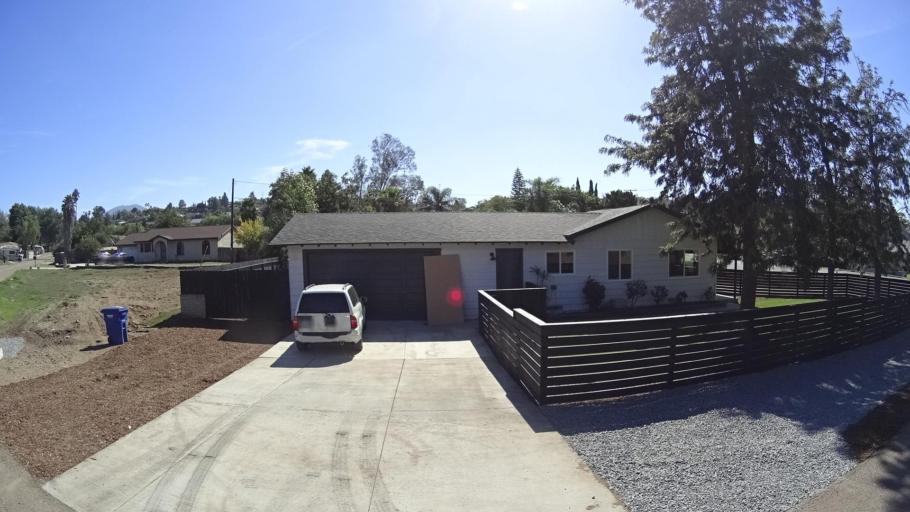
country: US
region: California
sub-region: San Diego County
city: Casa de Oro-Mount Helix
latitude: 32.7466
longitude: -116.9787
